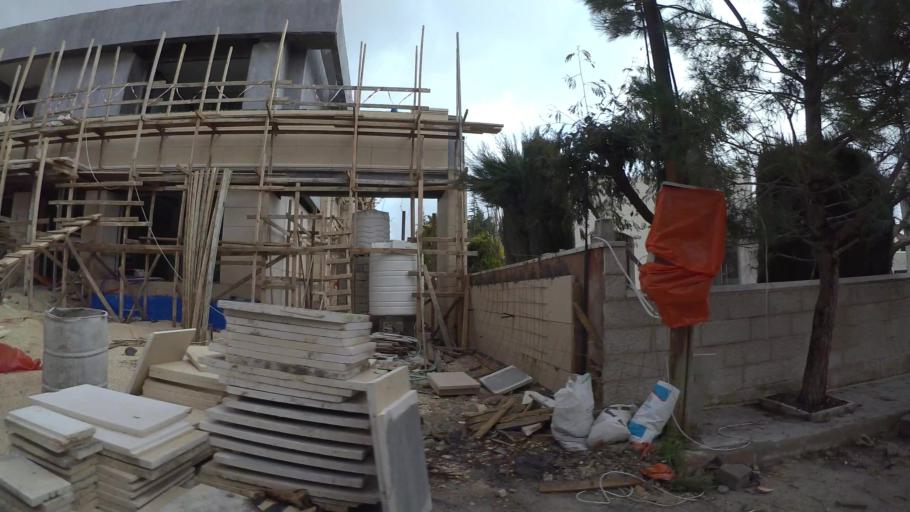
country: JO
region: Amman
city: Al Bunayyat ash Shamaliyah
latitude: 31.9512
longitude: 35.8800
